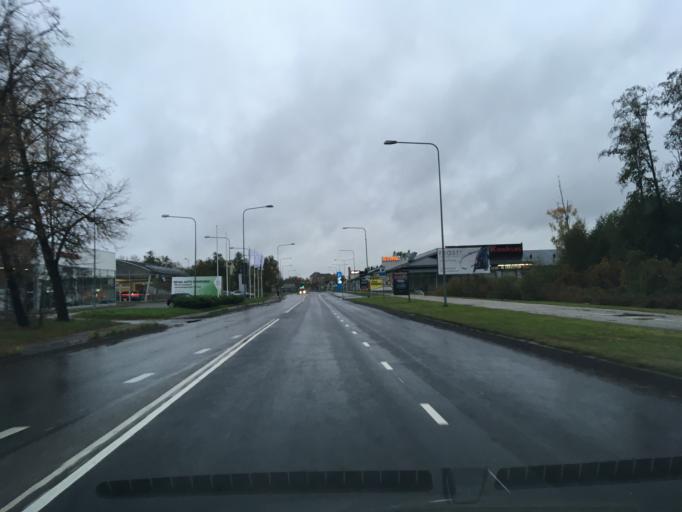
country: EE
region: Paernumaa
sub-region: Paernu linn
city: Parnu
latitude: 58.4060
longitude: 24.4931
